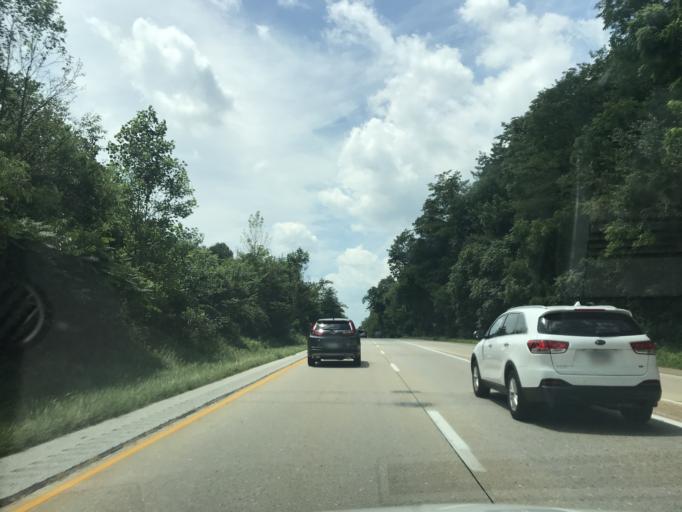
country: US
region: Pennsylvania
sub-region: Chester County
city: Kennett Square
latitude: 39.8563
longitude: -75.7187
